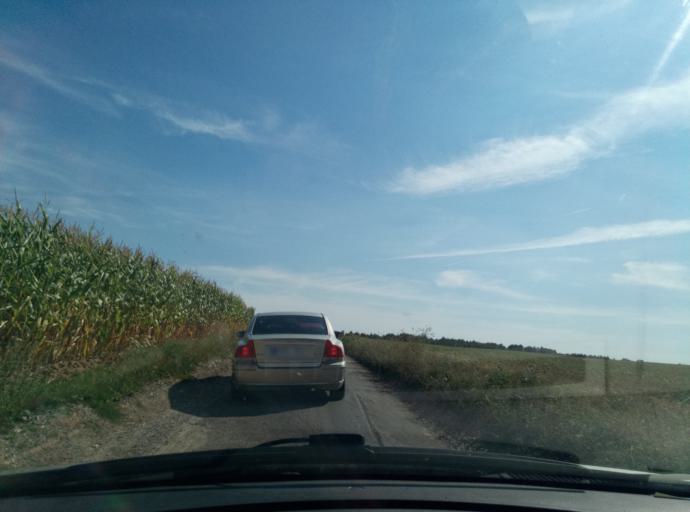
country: PL
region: Kujawsko-Pomorskie
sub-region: Powiat brodnicki
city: Jablonowo Pomorskie
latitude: 53.4125
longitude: 19.2366
